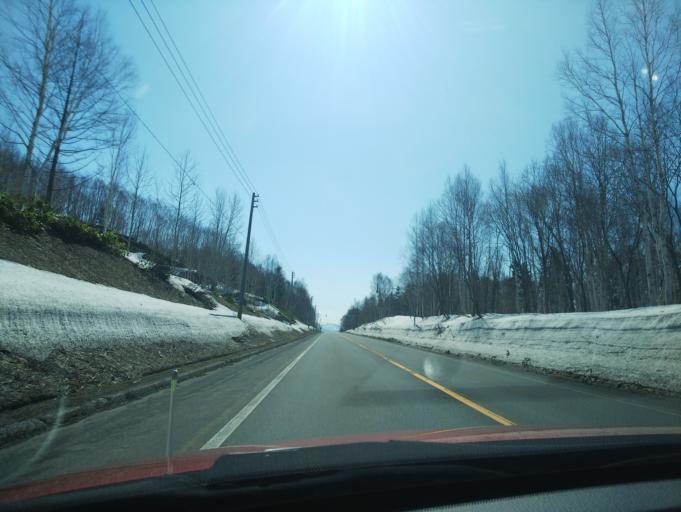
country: JP
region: Hokkaido
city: Nayoro
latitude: 44.6430
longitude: 142.2683
